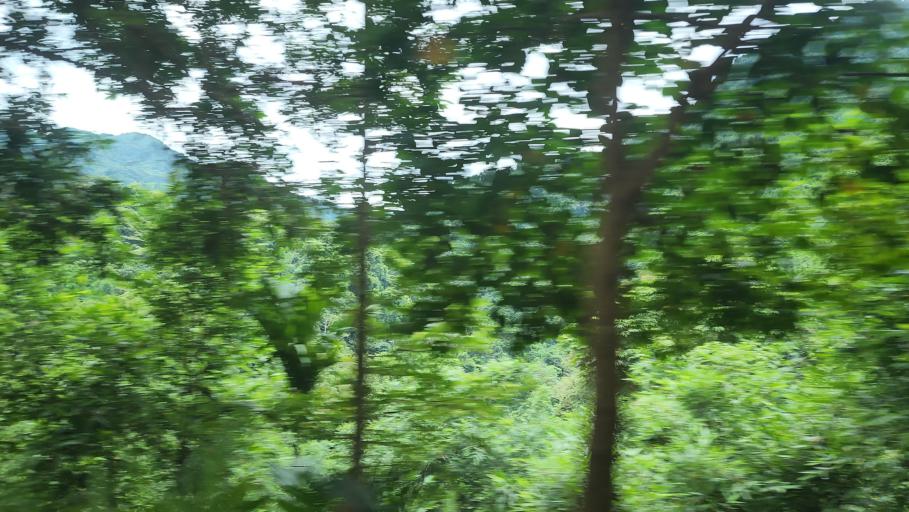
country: TW
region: Taiwan
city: Daxi
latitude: 24.8729
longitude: 121.3854
